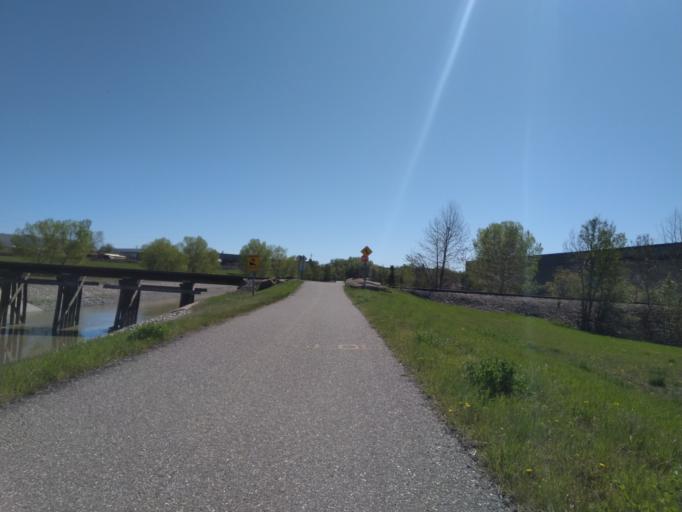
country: CA
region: Alberta
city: Calgary
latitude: 51.0018
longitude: -114.0019
